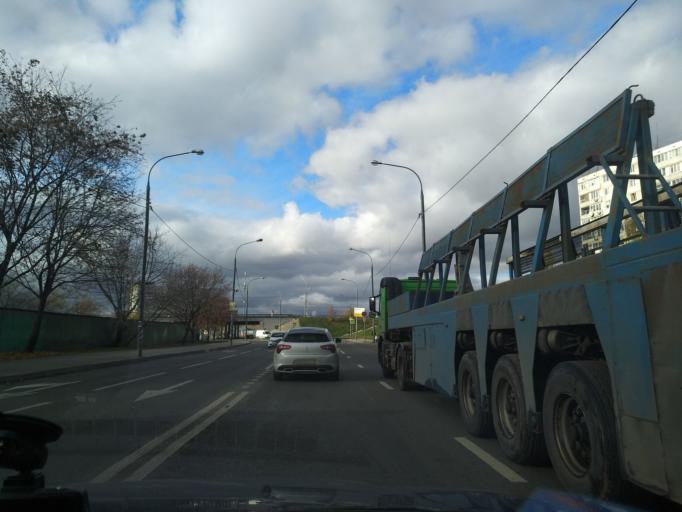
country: RU
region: Moscow
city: Slobodka
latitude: 55.8696
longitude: 37.5881
